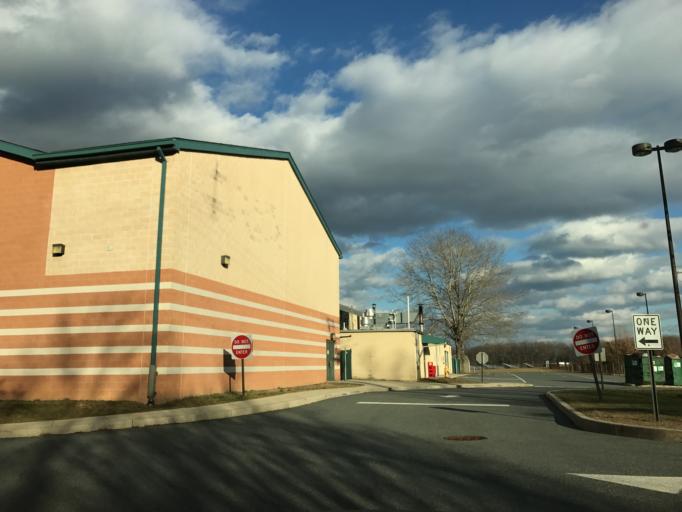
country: US
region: Maryland
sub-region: Cecil County
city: North East
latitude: 39.6381
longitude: -75.9576
